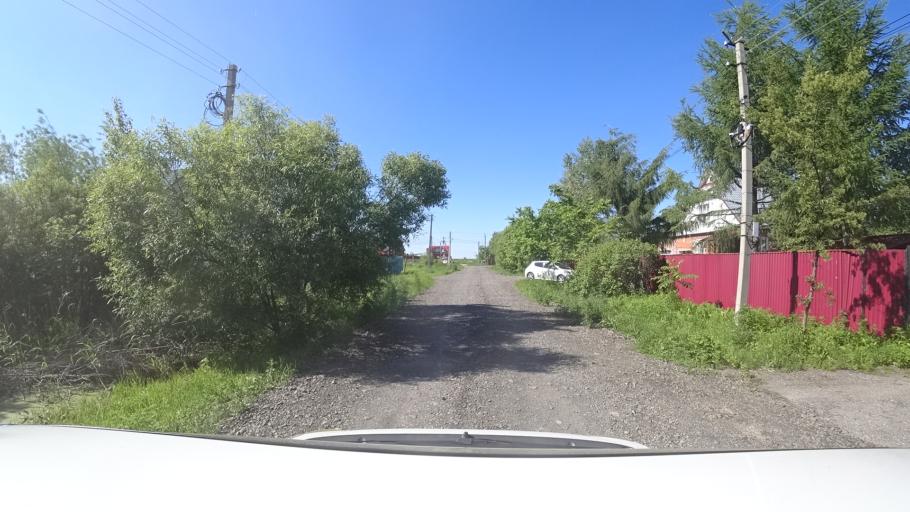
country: RU
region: Khabarovsk Krai
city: Topolevo
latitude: 48.5520
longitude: 135.1725
